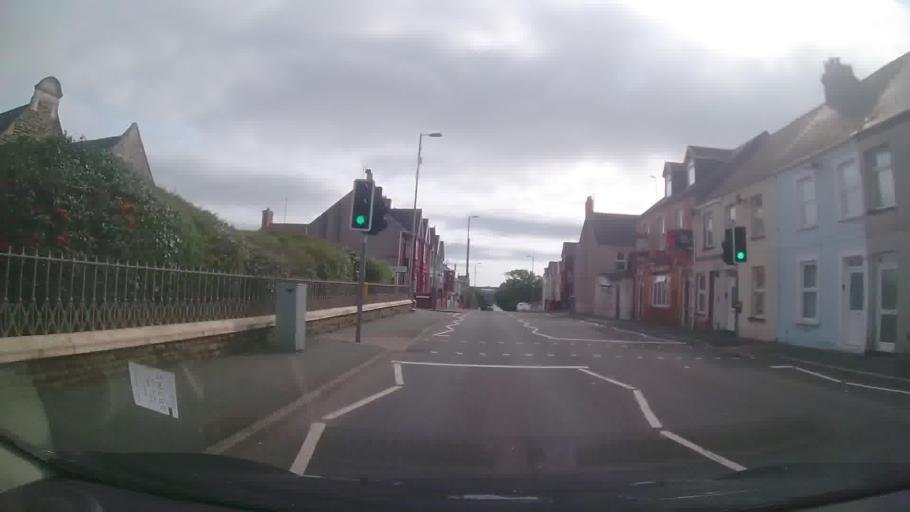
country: GB
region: Wales
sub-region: Pembrokeshire
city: Milford Haven
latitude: 51.7138
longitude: -5.0284
